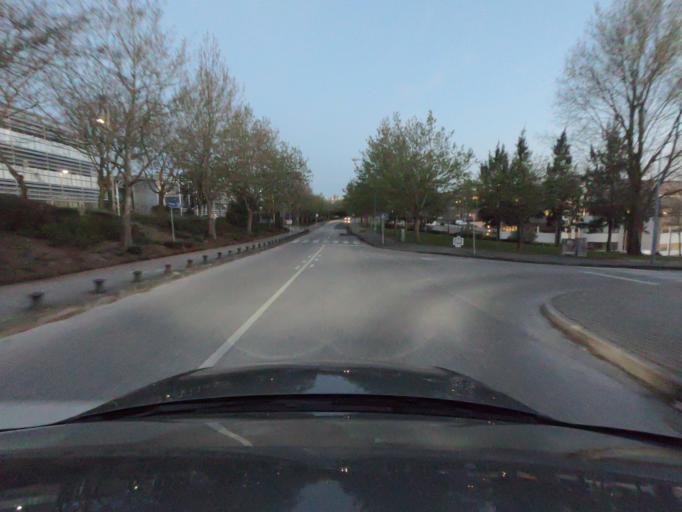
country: PT
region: Lisbon
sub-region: Sintra
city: Cacem
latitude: 38.7445
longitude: -9.3042
